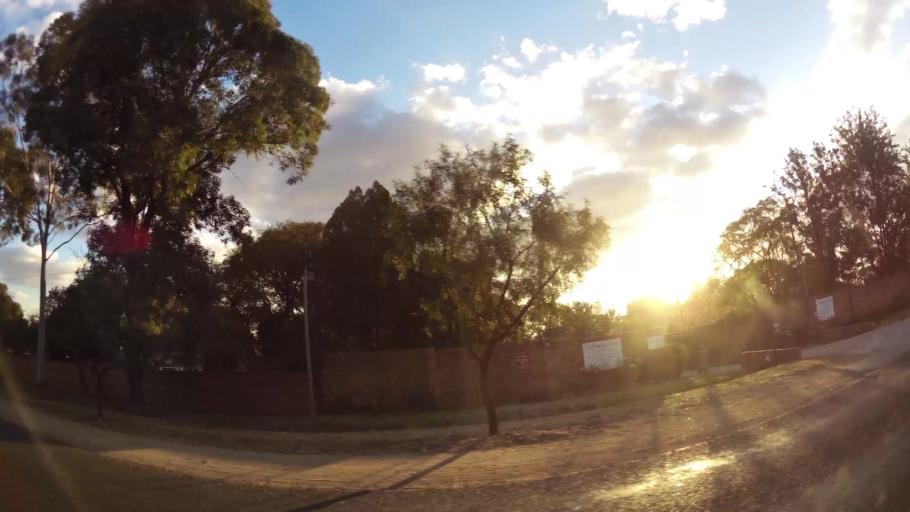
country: ZA
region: Gauteng
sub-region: City of Johannesburg Metropolitan Municipality
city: Midrand
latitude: -25.9721
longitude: 28.1533
